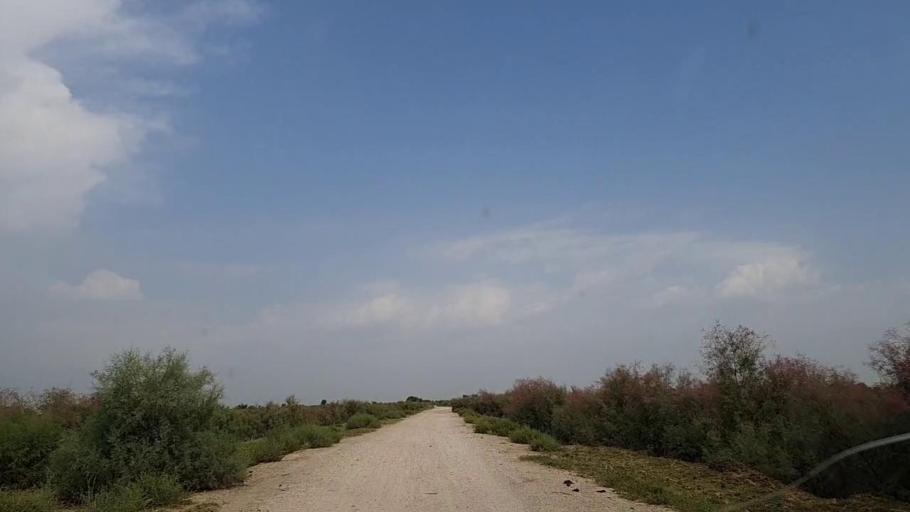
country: PK
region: Sindh
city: Khanpur
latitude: 27.8289
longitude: 69.5113
